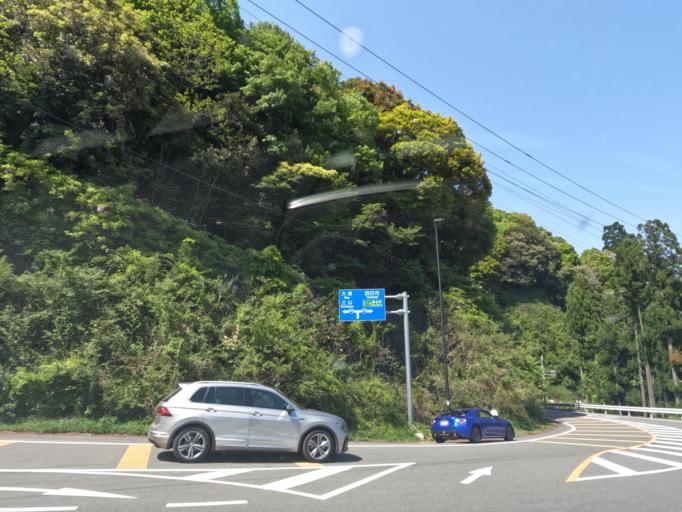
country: JP
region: Mie
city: Komono
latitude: 35.0196
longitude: 136.4511
